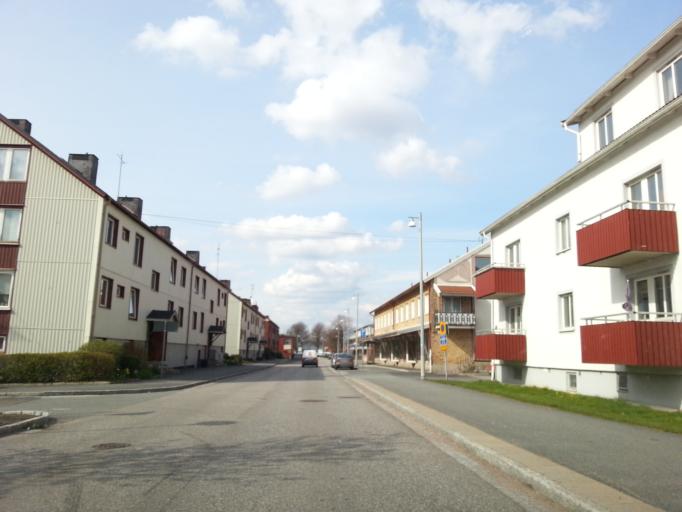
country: SE
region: Vaestra Goetaland
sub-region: Ale Kommun
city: Surte
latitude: 57.8263
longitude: 12.0155
